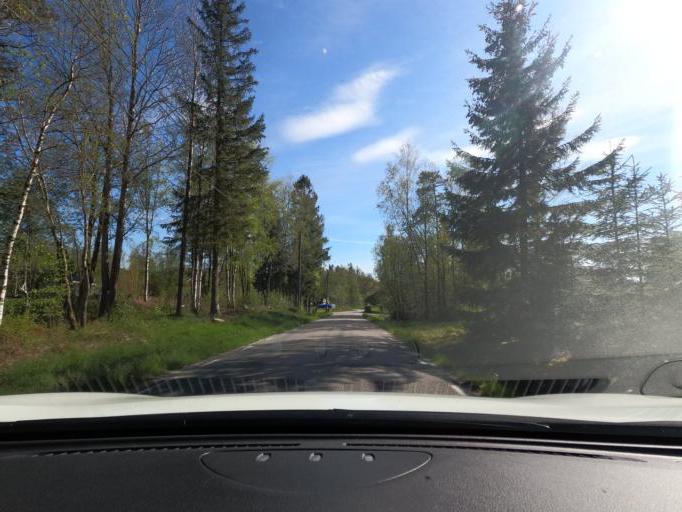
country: SE
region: Vaestra Goetaland
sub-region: Harryda Kommun
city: Hindas
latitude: 57.6477
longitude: 12.3565
